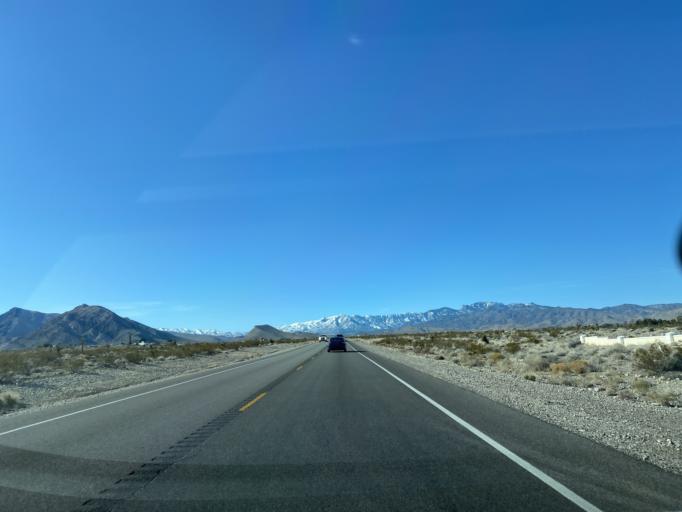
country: US
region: Nevada
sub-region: Clark County
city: Summerlin South
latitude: 36.3233
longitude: -115.3484
